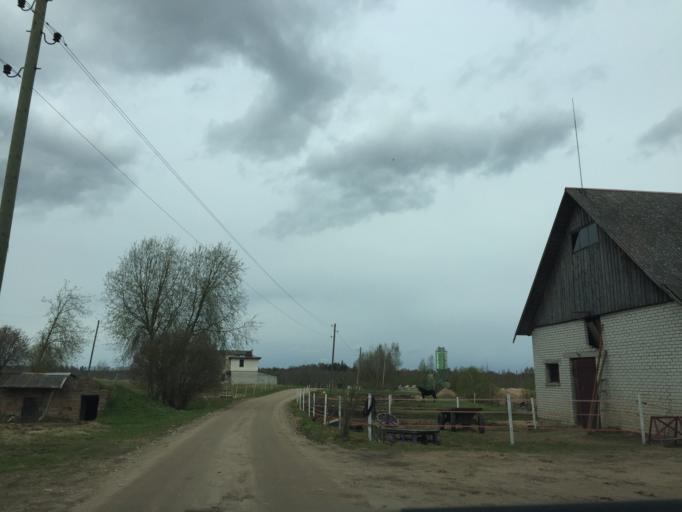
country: LV
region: Priekuli
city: Priekuli
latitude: 57.3156
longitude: 25.3628
